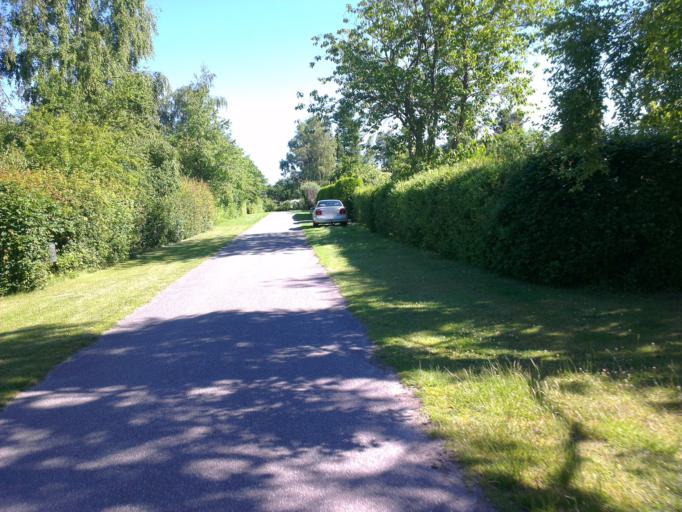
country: DK
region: Capital Region
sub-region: Halsnaes Kommune
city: Hundested
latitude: 55.9274
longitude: 11.9103
